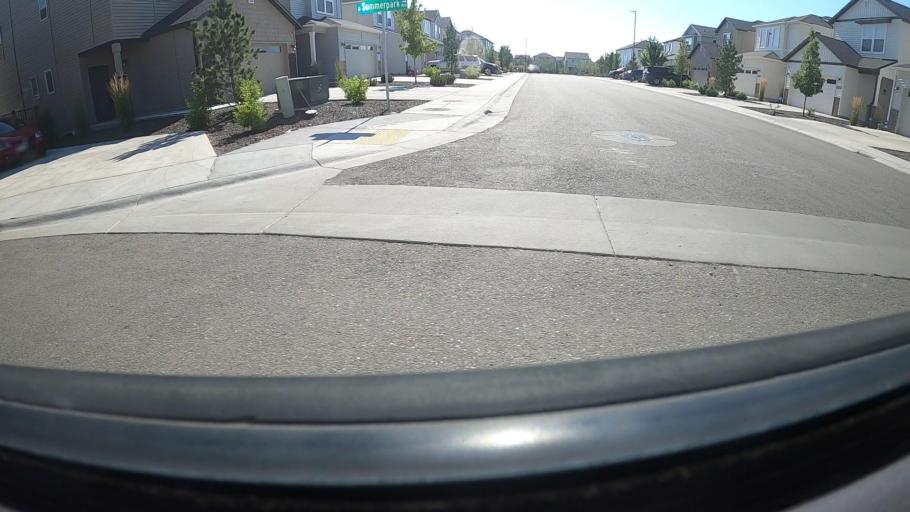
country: US
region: Idaho
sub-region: Ada County
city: Meridian
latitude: 43.6327
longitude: -116.3686
